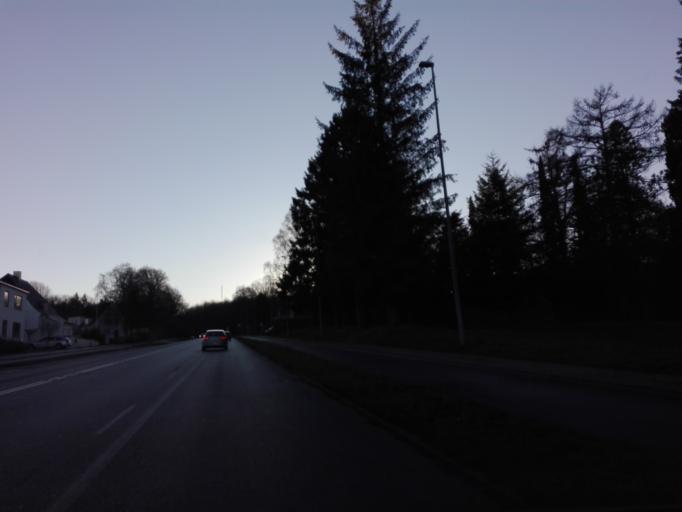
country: DK
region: Central Jutland
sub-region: Arhus Kommune
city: Arhus
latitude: 56.1279
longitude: 10.2110
